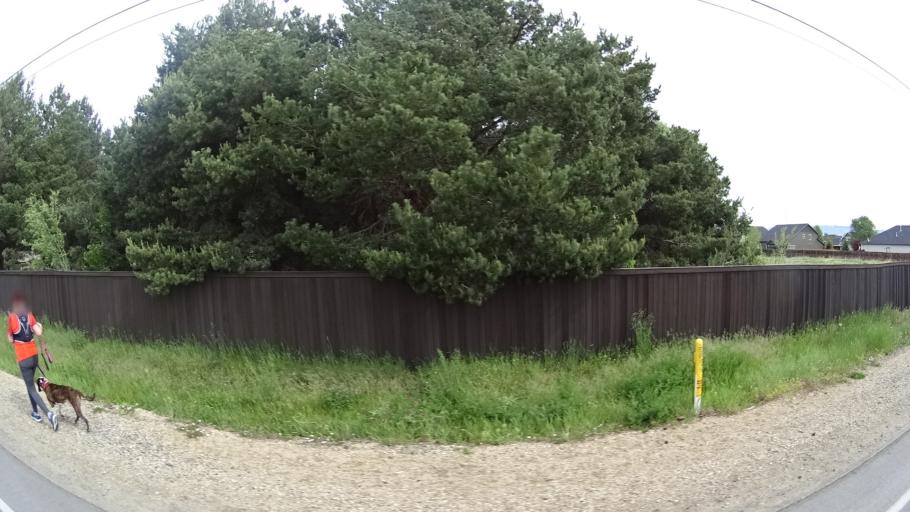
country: US
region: Idaho
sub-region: Ada County
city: Garden City
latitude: 43.5465
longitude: -116.3101
